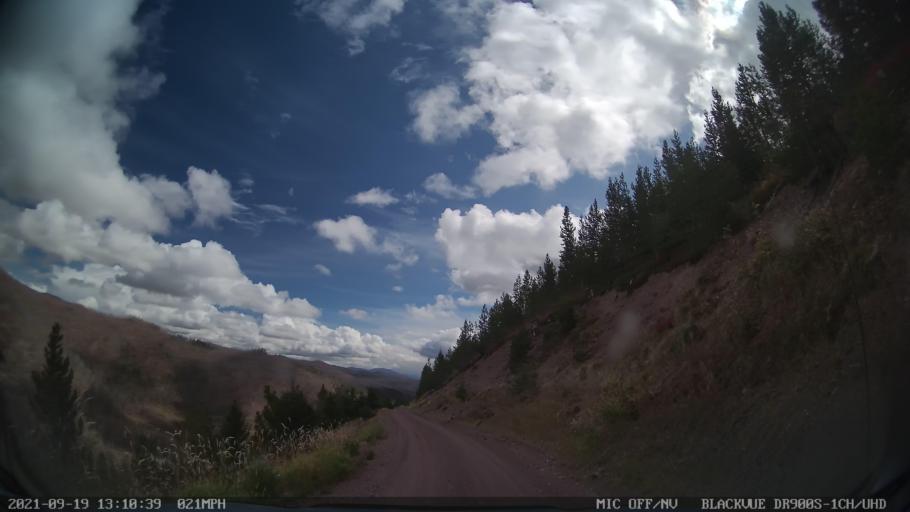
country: US
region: Montana
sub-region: Missoula County
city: Seeley Lake
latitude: 47.1773
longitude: -113.3506
